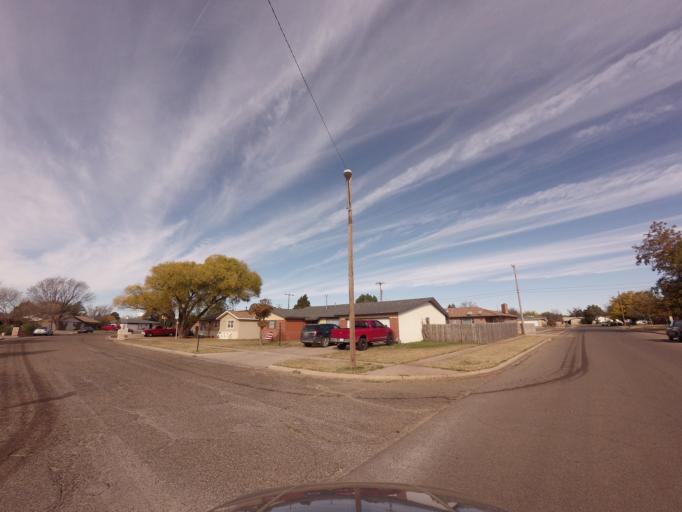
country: US
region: New Mexico
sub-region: Curry County
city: Clovis
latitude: 34.4245
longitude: -103.2191
